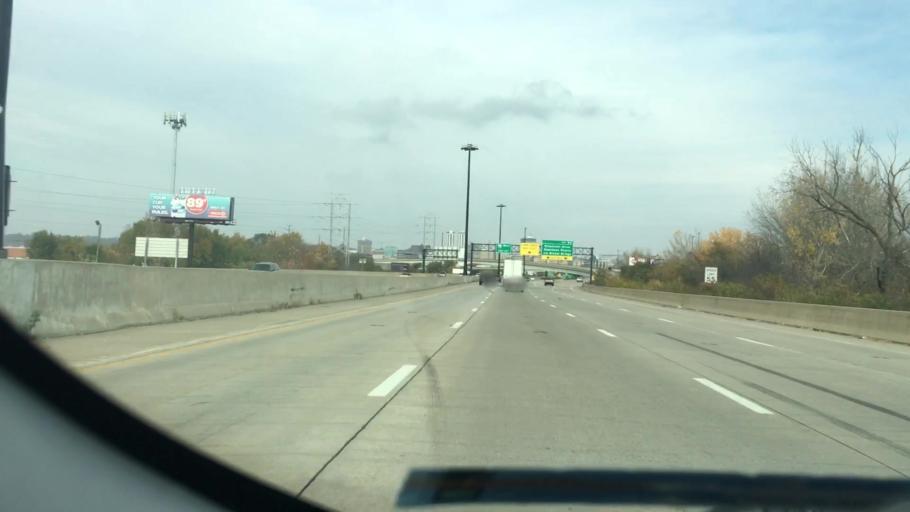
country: US
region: Illinois
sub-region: Tazewell County
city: East Peoria
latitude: 40.6754
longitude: -89.5772
